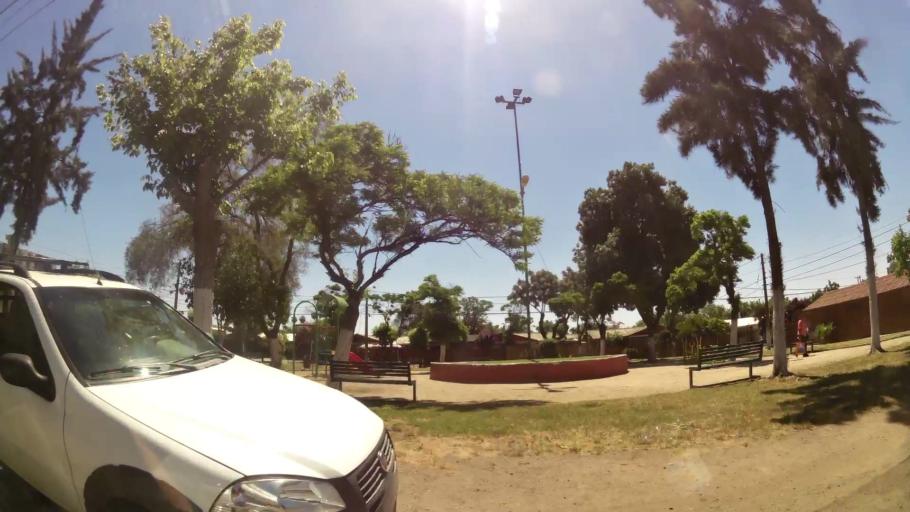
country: CL
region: Santiago Metropolitan
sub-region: Provincia de Maipo
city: San Bernardo
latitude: -33.5745
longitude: -70.6880
